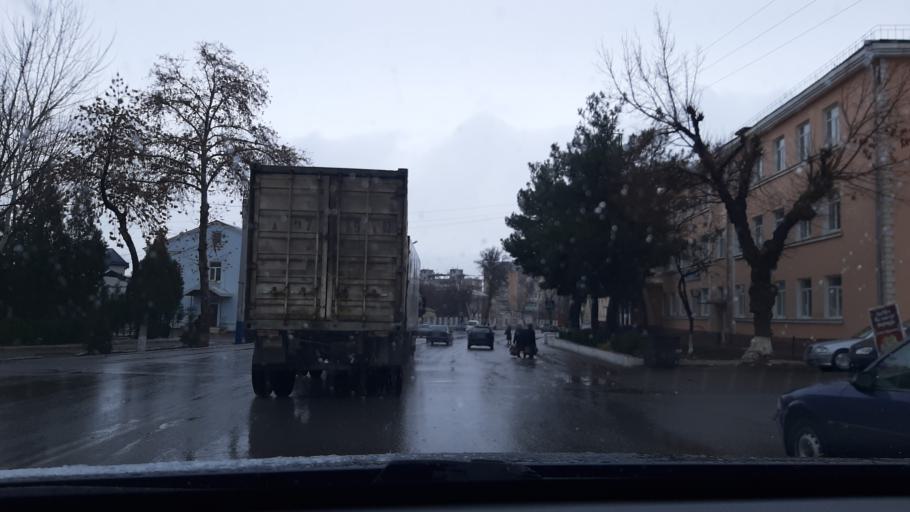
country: TJ
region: Viloyati Sughd
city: Khujand
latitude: 40.2742
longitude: 69.6415
